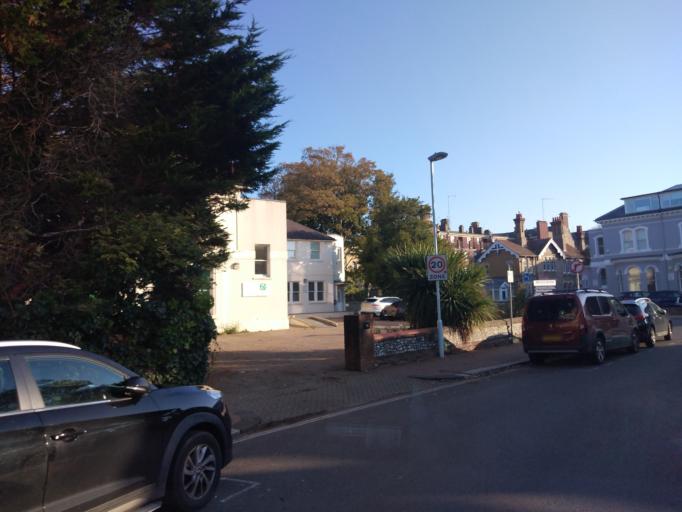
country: GB
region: England
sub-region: West Sussex
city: Worthing
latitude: 50.8128
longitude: -0.3722
